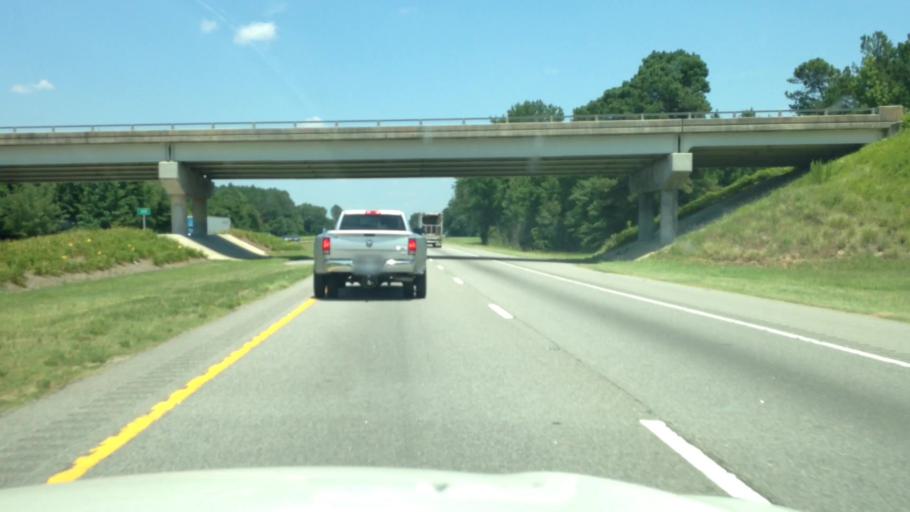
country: US
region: North Carolina
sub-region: Robeson County
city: Rowland
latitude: 34.5420
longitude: -79.2270
